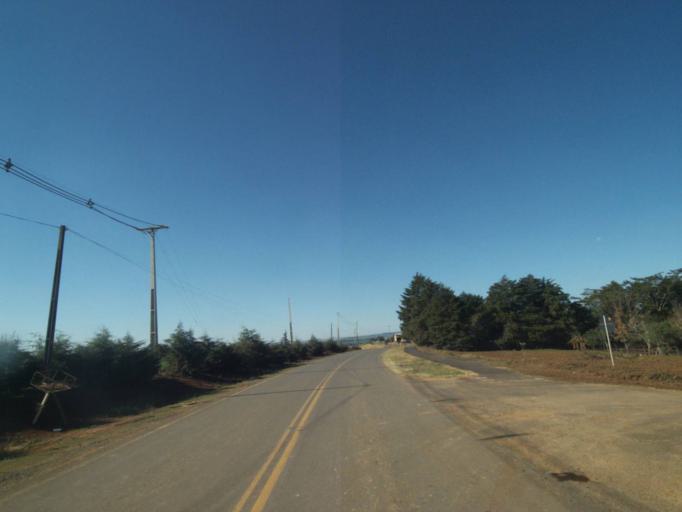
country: BR
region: Parana
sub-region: Tibagi
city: Tibagi
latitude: -24.5232
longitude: -50.4319
